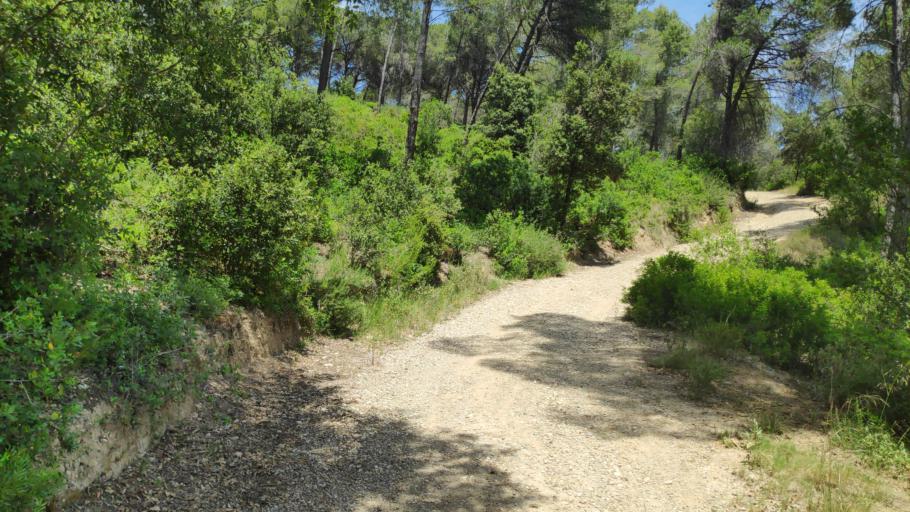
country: ES
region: Catalonia
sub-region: Provincia de Barcelona
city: Rubi
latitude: 41.5037
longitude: 2.0593
